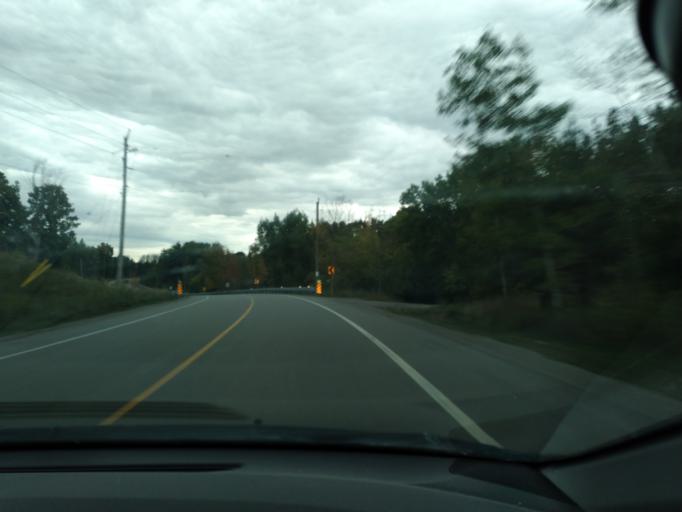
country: CA
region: Ontario
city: Brampton
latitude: 43.9335
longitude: -79.7984
